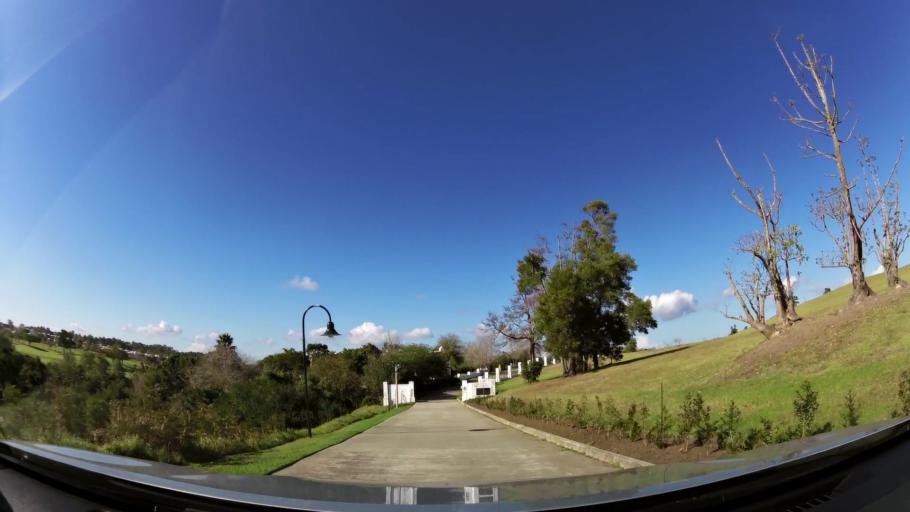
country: ZA
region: Western Cape
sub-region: Eden District Municipality
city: George
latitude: -33.9621
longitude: 22.4050
